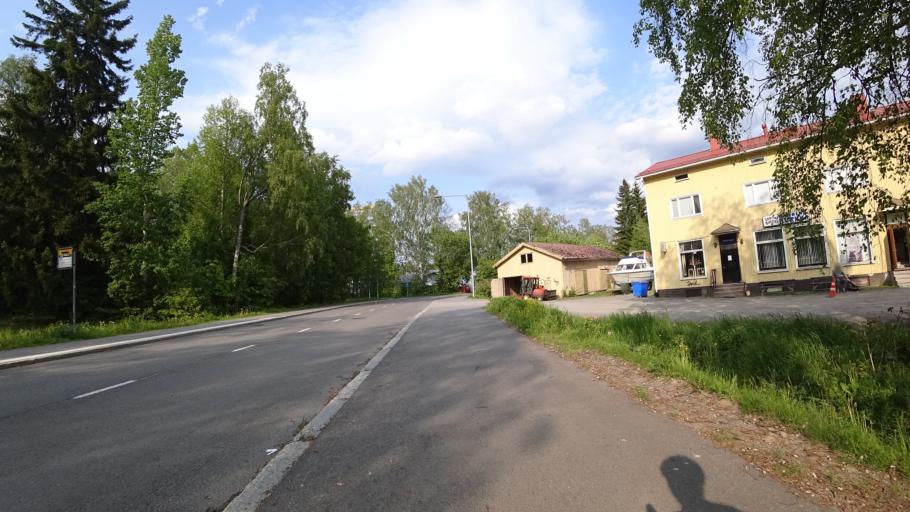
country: FI
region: Pirkanmaa
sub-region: Tampere
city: Pirkkala
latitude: 61.5022
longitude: 23.6296
